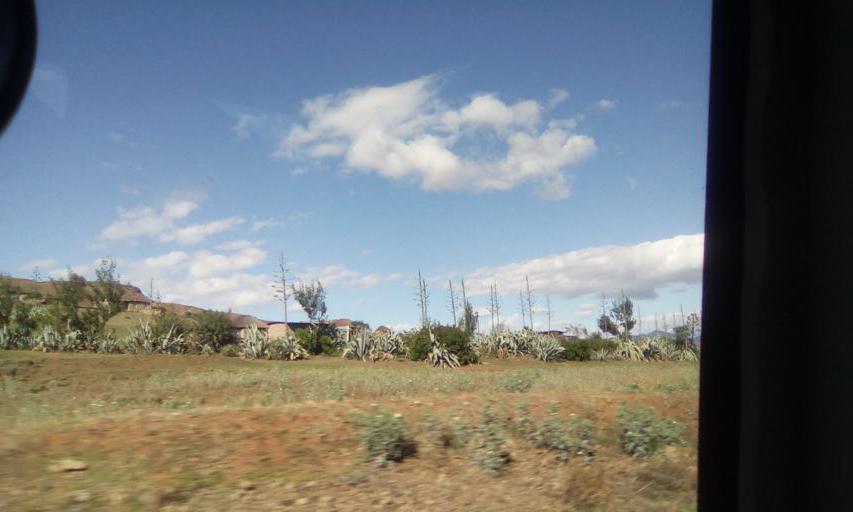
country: LS
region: Qacha's Nek
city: Qacha's Nek
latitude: -30.0480
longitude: 28.2834
